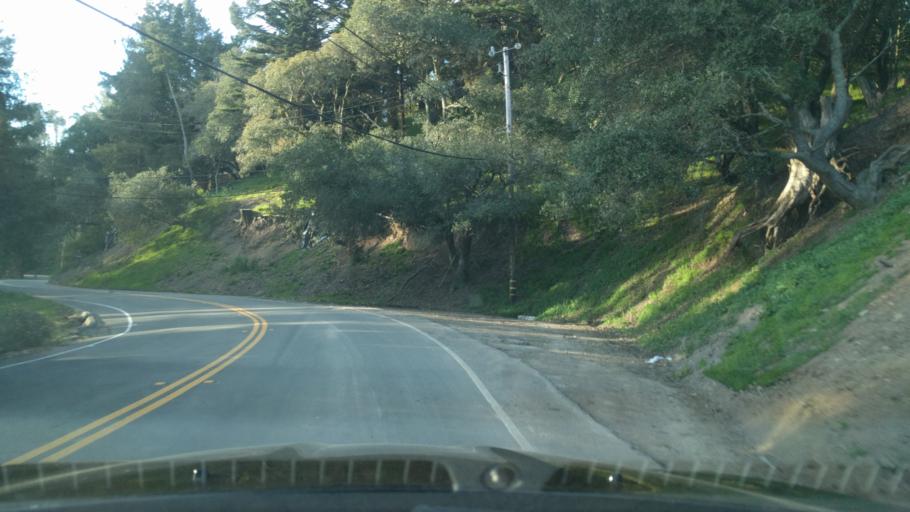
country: US
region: California
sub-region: Contra Costa County
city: Orinda
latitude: 37.8377
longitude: -122.1910
